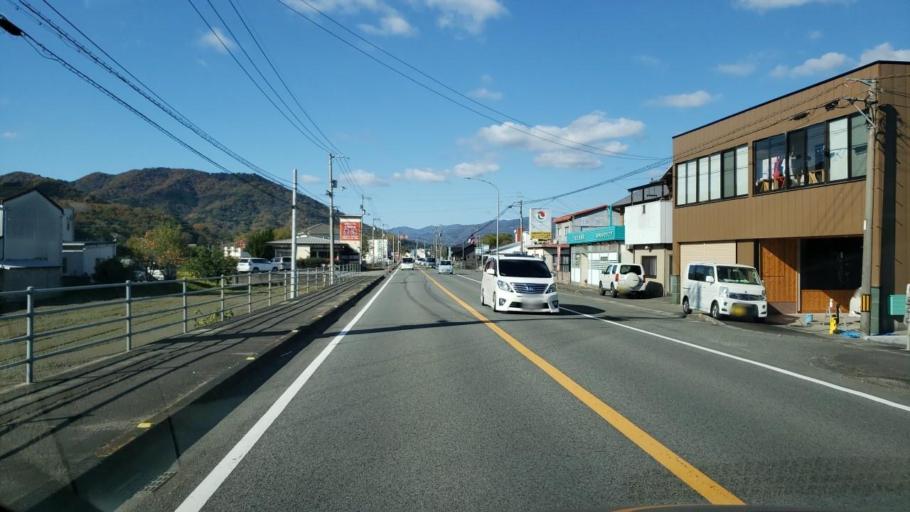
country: JP
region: Tokushima
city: Wakimachi
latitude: 34.0579
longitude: 134.2246
